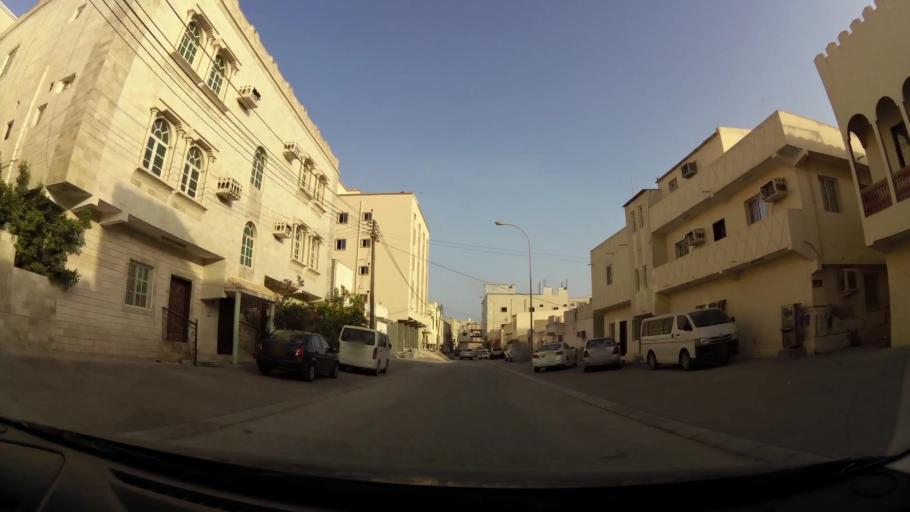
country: OM
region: Zufar
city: Salalah
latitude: 17.0141
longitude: 54.0943
